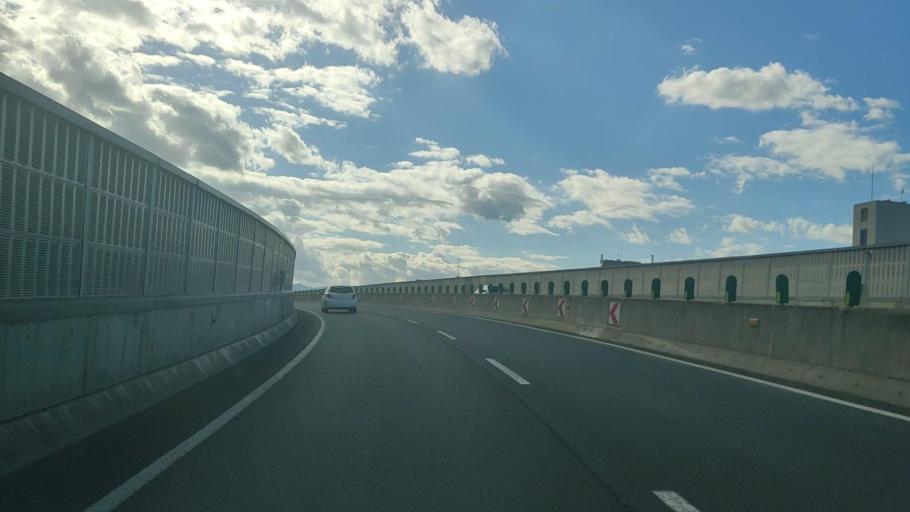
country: JP
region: Yamaguchi
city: Shimonoseki
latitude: 33.8840
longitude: 130.9069
